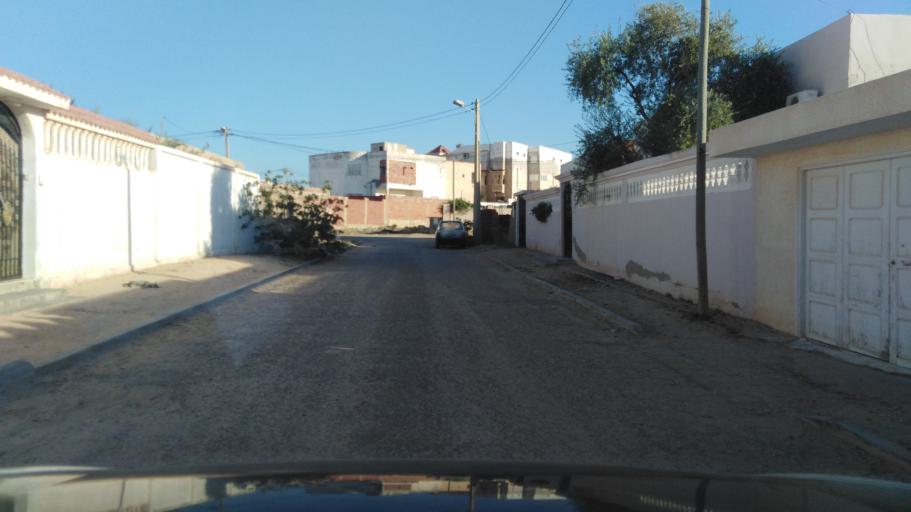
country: TN
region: Qabis
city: Gabes
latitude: 33.9521
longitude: 10.0113
